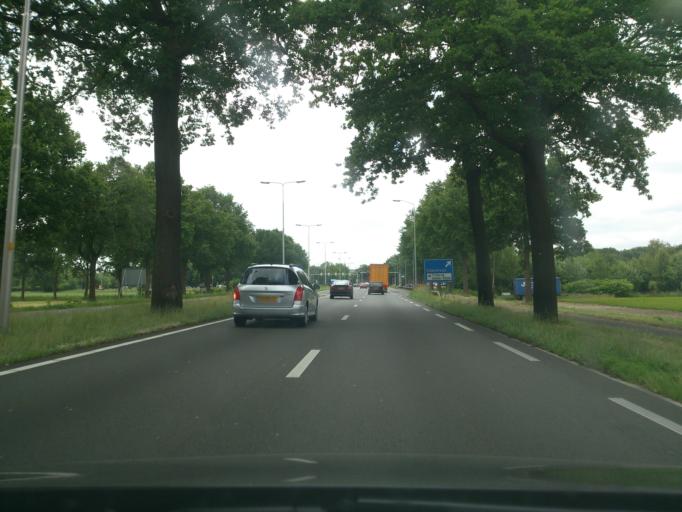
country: NL
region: North Brabant
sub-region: Gemeente Oisterwijk
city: Oisterwijk
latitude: 51.5951
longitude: 5.1746
